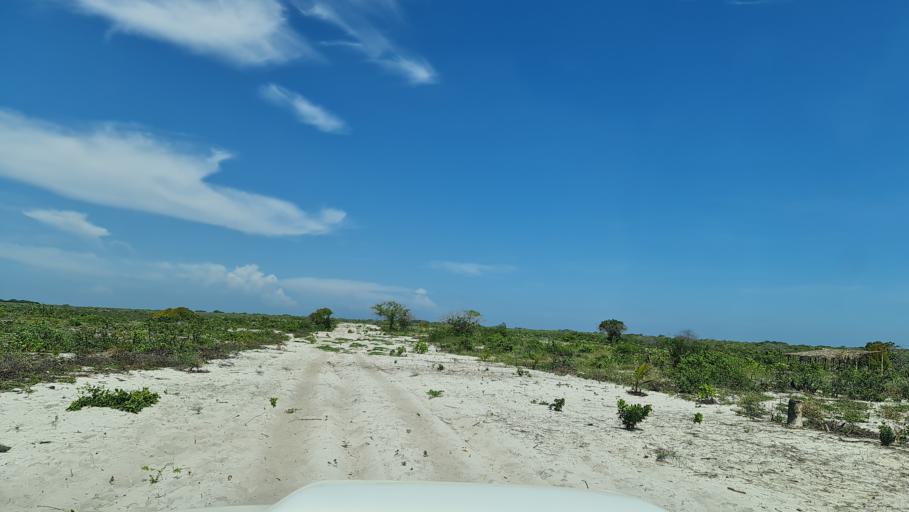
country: MZ
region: Nampula
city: Ilha de Mocambique
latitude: -15.1945
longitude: 40.6211
